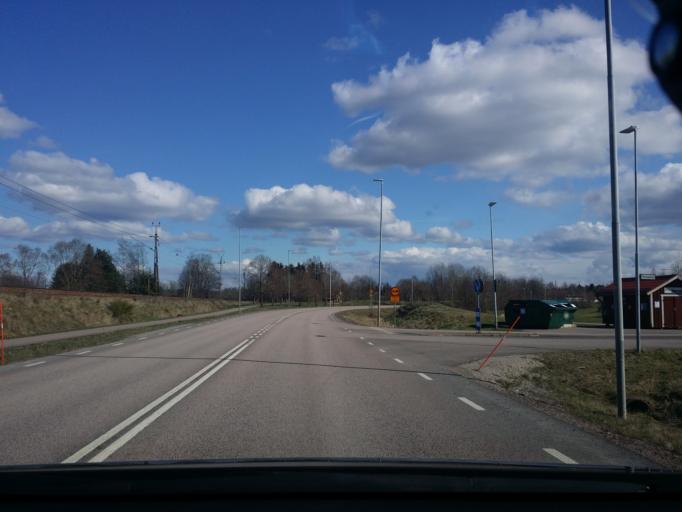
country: SE
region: Vaestmanland
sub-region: Sala Kommun
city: Sala
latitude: 59.9357
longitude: 16.5711
